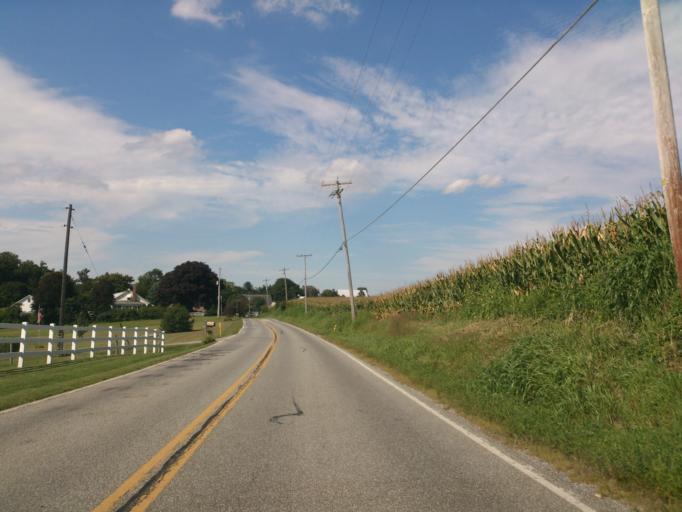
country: US
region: Pennsylvania
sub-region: York County
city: Susquehanna Trails
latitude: 39.7638
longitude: -76.4680
